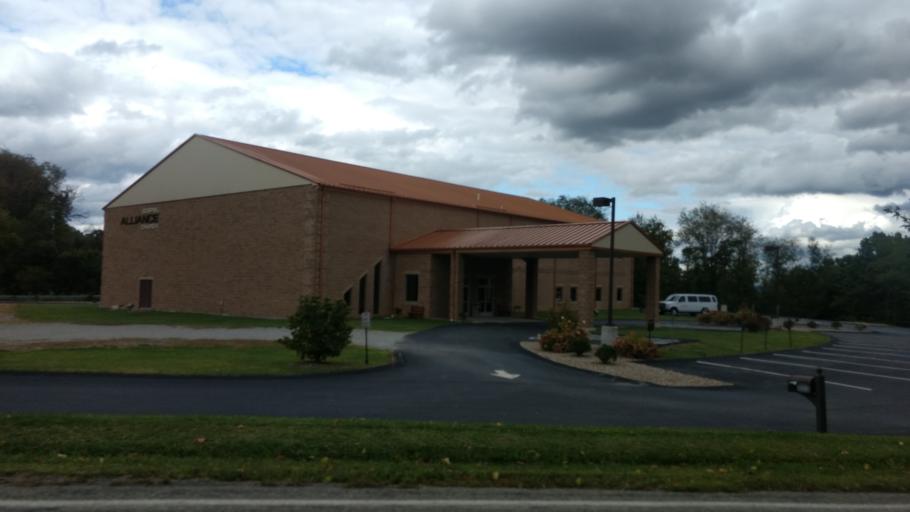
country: US
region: Pennsylvania
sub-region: Westmoreland County
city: Fellsburg
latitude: 40.1959
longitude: -79.8300
